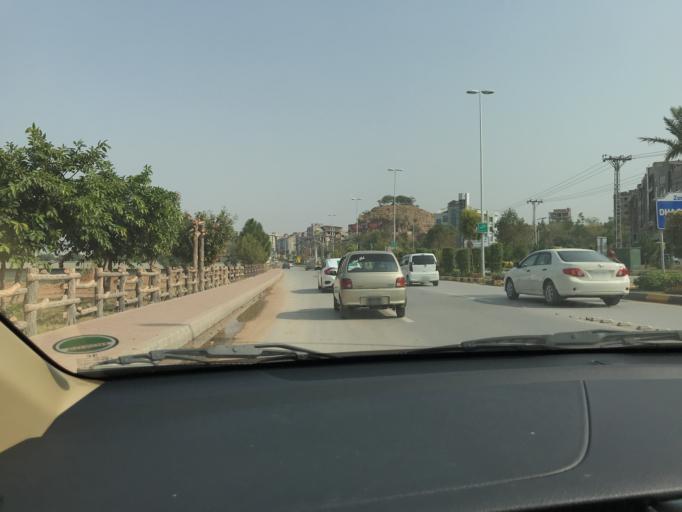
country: PK
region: Punjab
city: Rawalpindi
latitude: 33.5219
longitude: 73.1024
